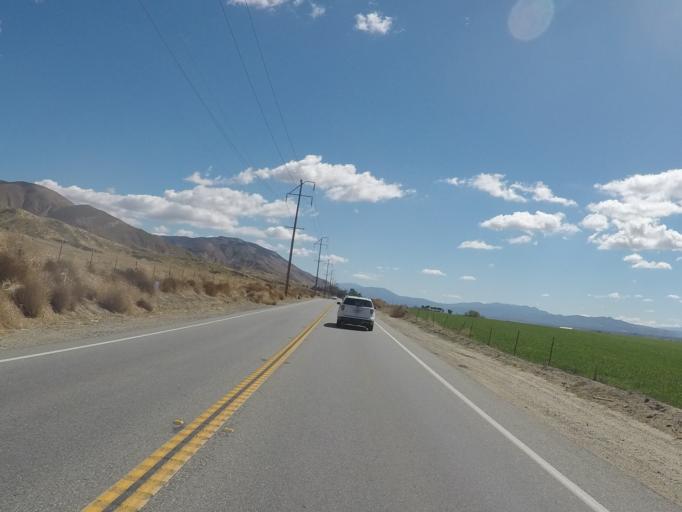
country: US
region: California
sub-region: Riverside County
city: Beaumont
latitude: 33.8641
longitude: -117.0285
